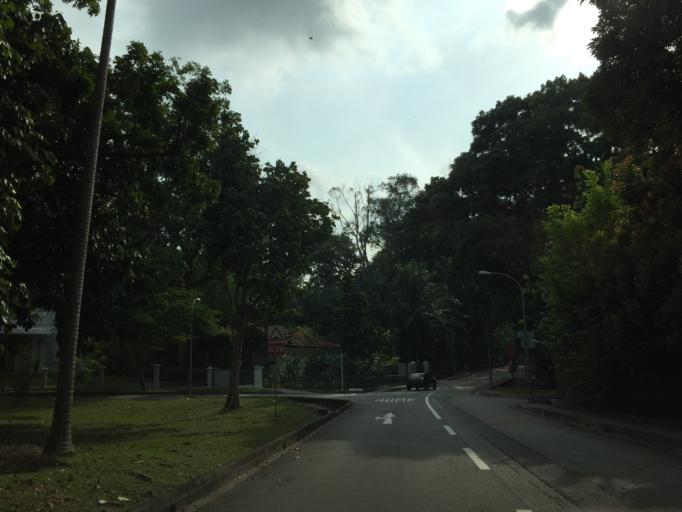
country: SG
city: Singapore
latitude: 1.3062
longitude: 103.8076
